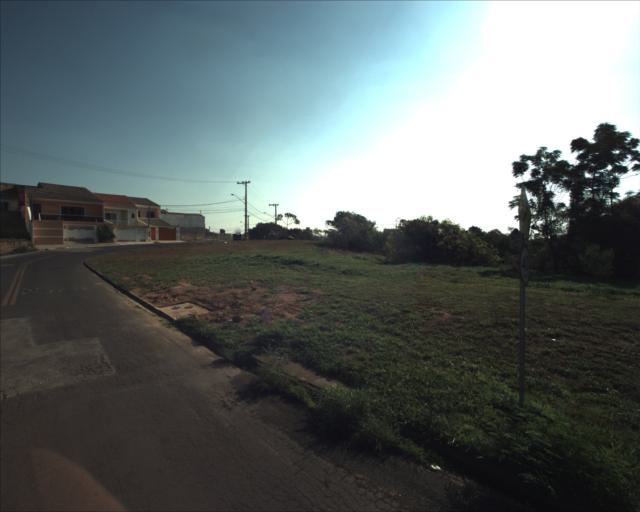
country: BR
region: Sao Paulo
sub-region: Sorocaba
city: Sorocaba
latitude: -23.4980
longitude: -47.4233
